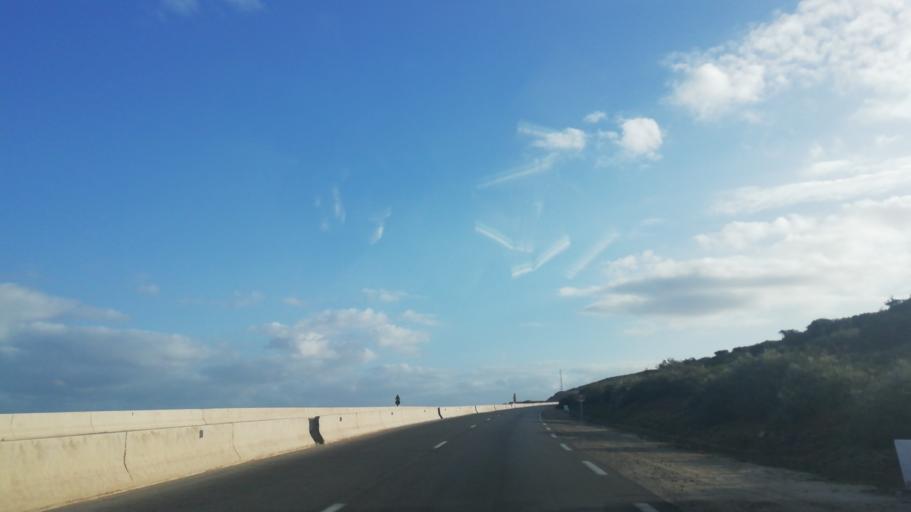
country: DZ
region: Mostaganem
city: Mostaganem
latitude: 36.1052
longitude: 0.2157
